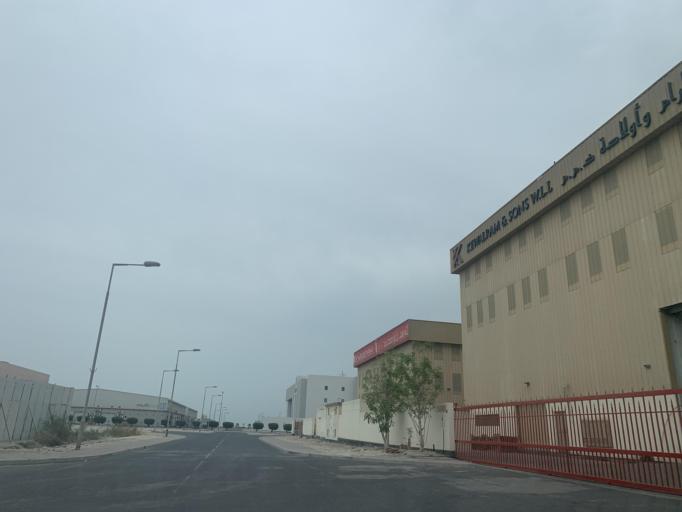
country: BH
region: Muharraq
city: Al Hadd
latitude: 26.2119
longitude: 50.6774
